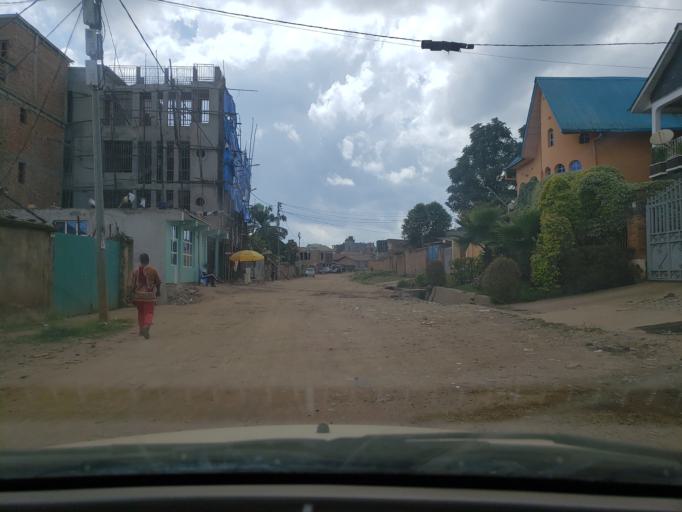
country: RW
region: Western Province
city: Cyangugu
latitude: -2.4974
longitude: 28.8870
